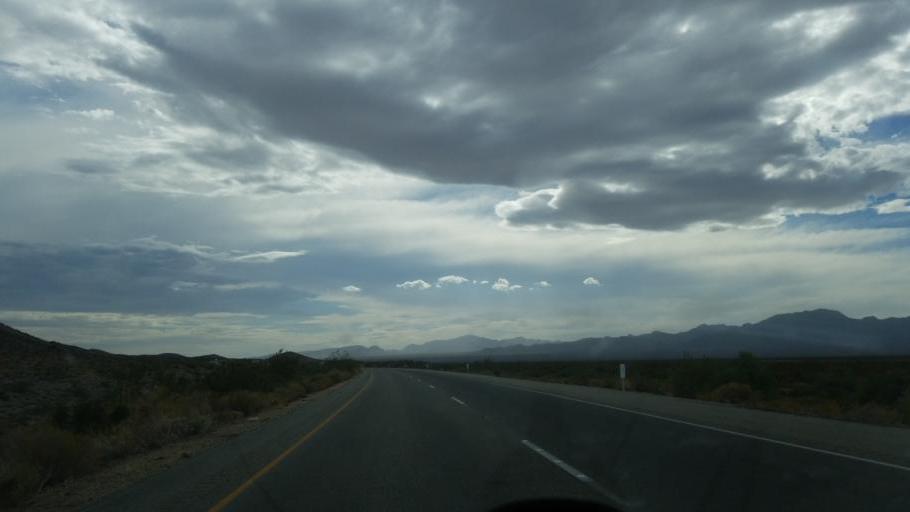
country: US
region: California
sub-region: San Bernardino County
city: Needles
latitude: 34.8038
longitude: -115.3684
